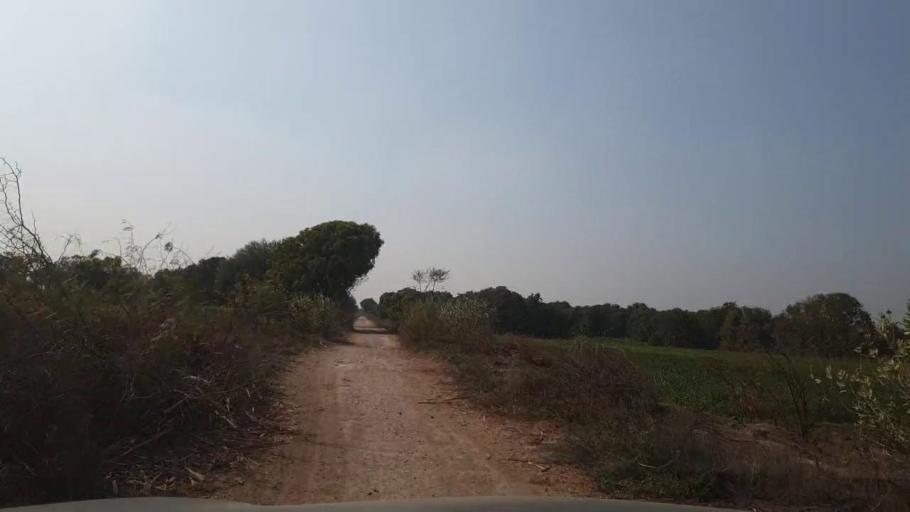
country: PK
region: Sindh
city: Tando Allahyar
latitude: 25.5933
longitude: 68.8190
